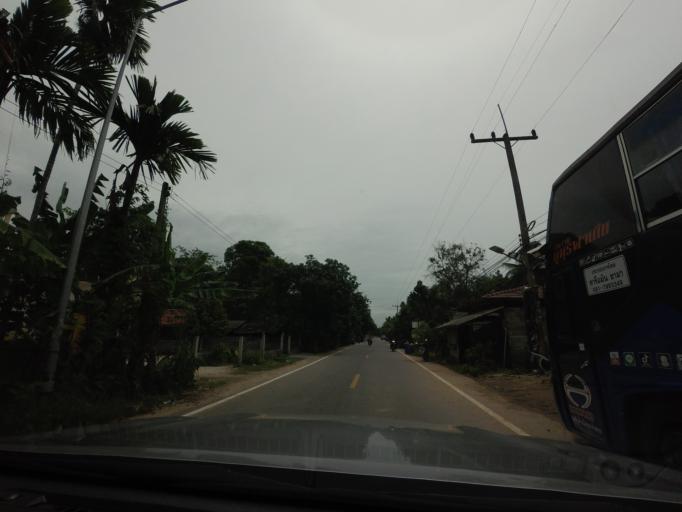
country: TH
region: Pattani
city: Kapho
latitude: 6.6191
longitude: 101.5429
